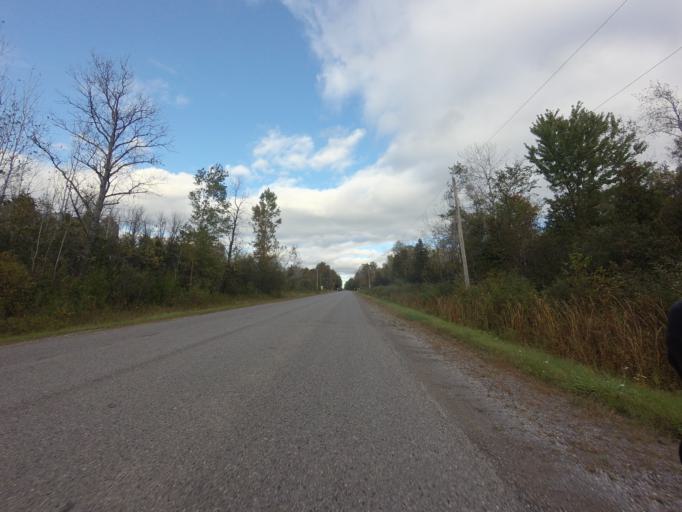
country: CA
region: Ontario
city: Cobourg
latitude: 43.9737
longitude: -78.0178
